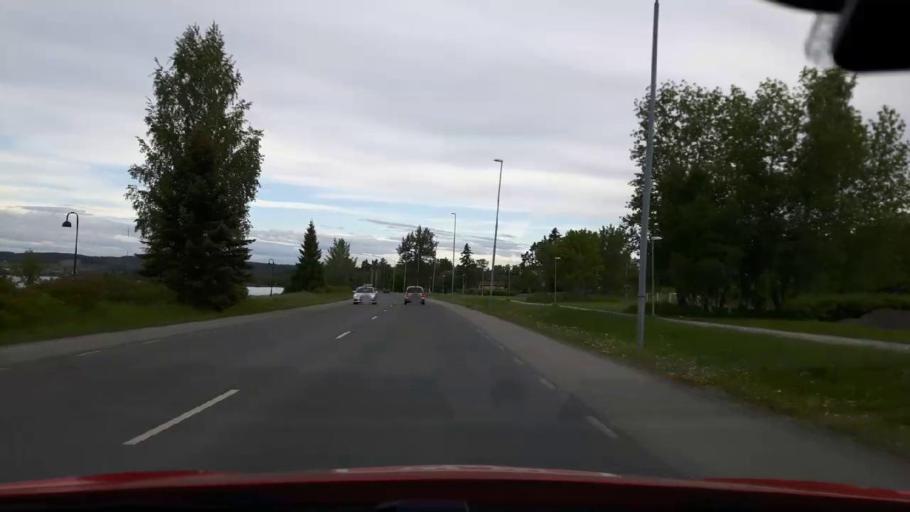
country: SE
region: Jaemtland
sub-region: OEstersunds Kommun
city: Ostersund
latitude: 63.1779
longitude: 14.6147
